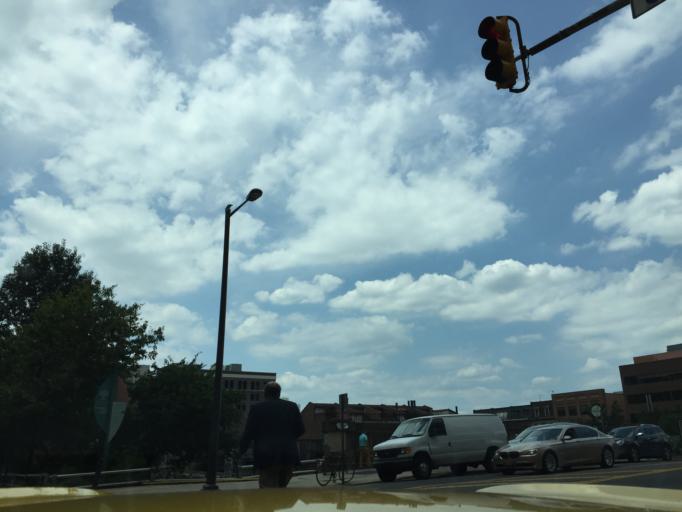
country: US
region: Pennsylvania
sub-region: Philadelphia County
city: Philadelphia
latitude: 39.9546
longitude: -75.1726
